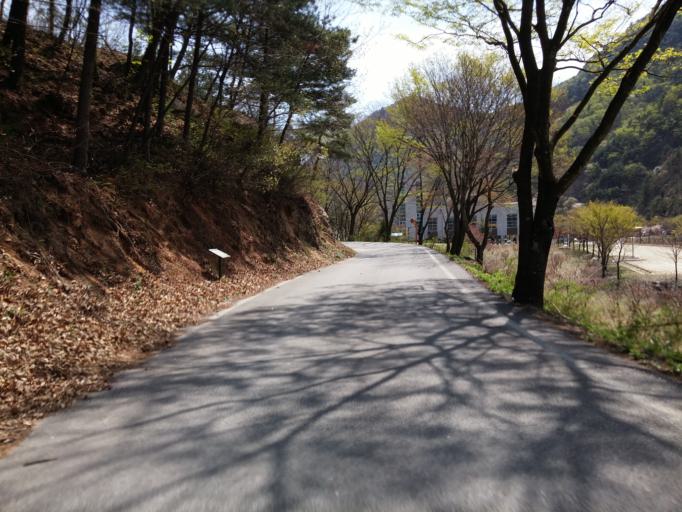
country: KR
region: Chungcheongbuk-do
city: Okcheon
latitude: 36.2467
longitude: 127.5544
